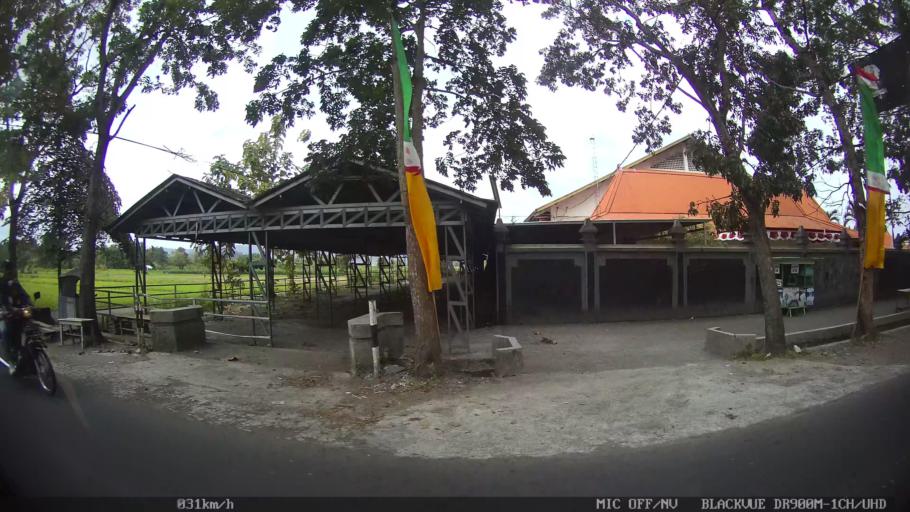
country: ID
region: Daerah Istimewa Yogyakarta
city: Depok
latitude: -7.8048
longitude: 110.4465
